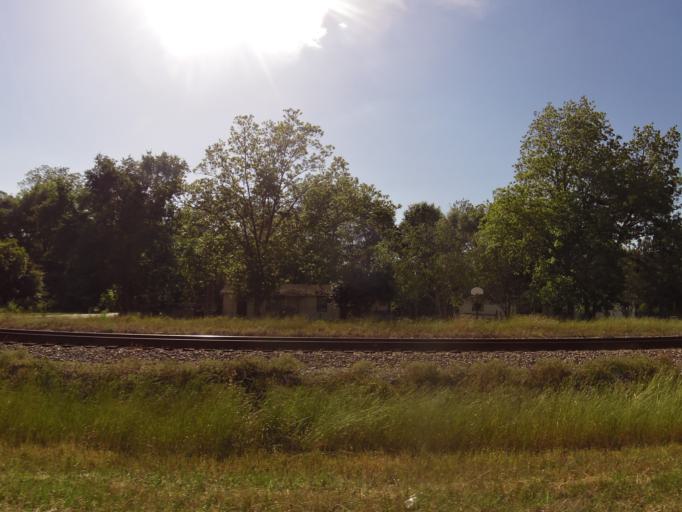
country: US
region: South Carolina
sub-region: Allendale County
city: Fairfax
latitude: 33.0380
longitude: -81.2216
